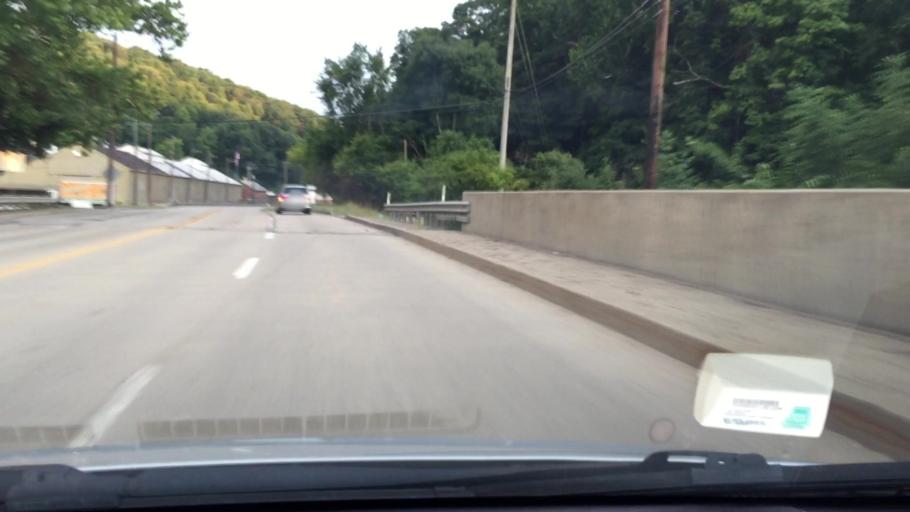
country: US
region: Pennsylvania
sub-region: Allegheny County
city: Allison Park
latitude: 40.5574
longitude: -79.9590
